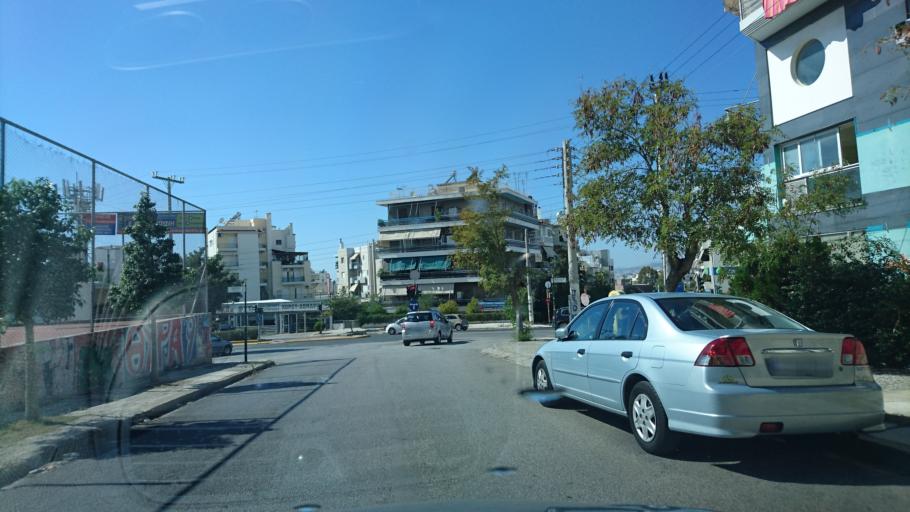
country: GR
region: Attica
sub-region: Nomarchia Athinas
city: Ilioupoli
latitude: 37.9369
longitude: 23.7596
